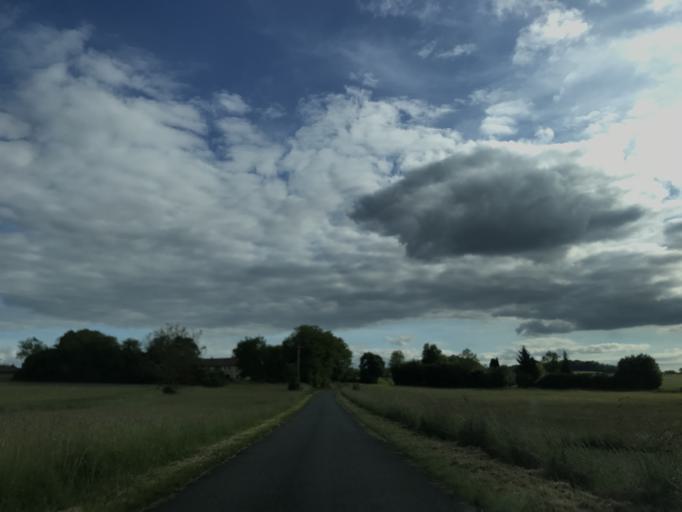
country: FR
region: Aquitaine
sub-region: Departement de la Dordogne
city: Saint-Aulaye
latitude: 45.2532
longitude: 0.1304
